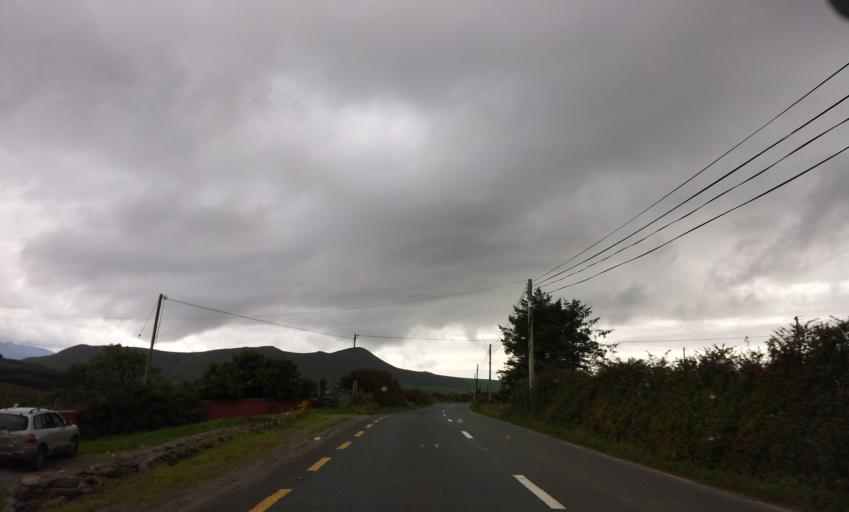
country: IE
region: Munster
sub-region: Ciarrai
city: Killorglin
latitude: 52.1864
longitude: -9.9546
